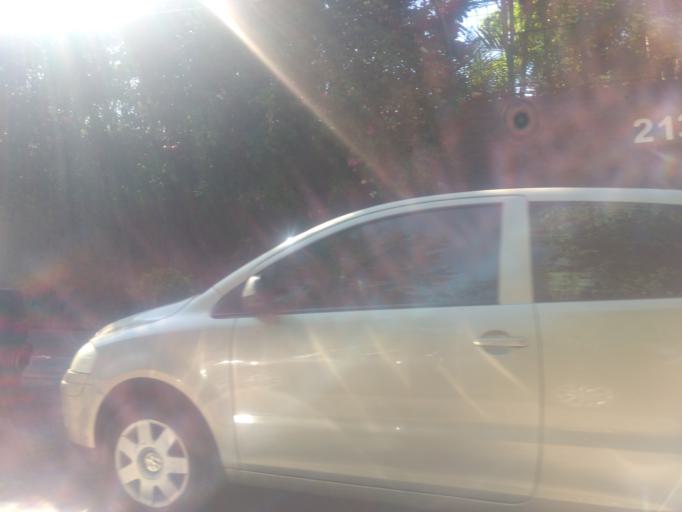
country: MX
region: Jalisco
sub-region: Zapopan
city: Zapopan
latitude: 20.6986
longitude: -103.3769
